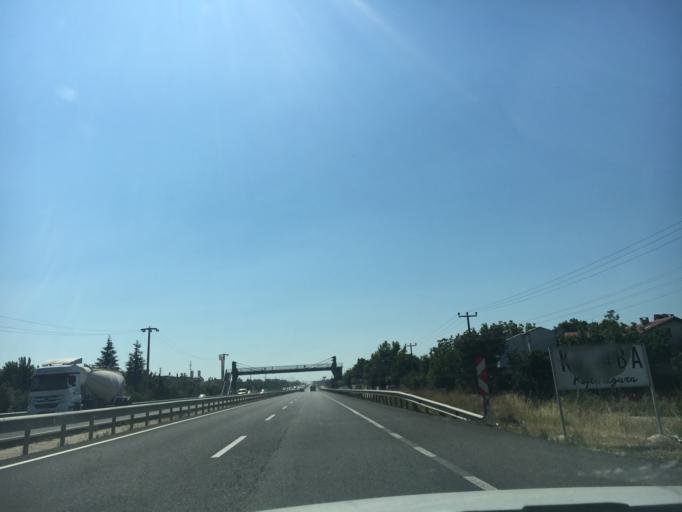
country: TR
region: Tekirdag
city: Marmara Ereglisi
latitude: 40.9879
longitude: 27.8533
